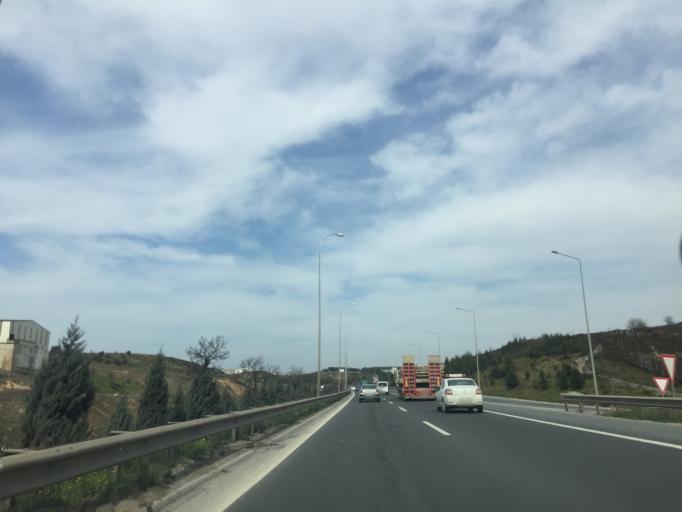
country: TR
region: Kocaeli
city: Balcik
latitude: 40.8409
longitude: 29.3735
